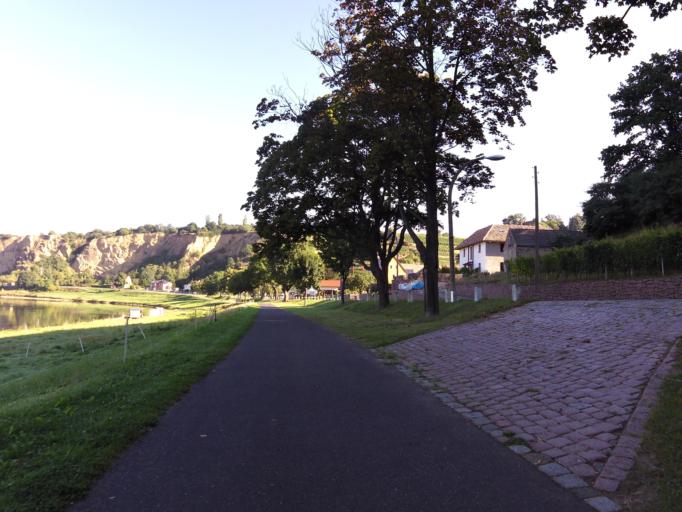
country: DE
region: Saxony
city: Weissig
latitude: 51.2309
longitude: 13.4270
